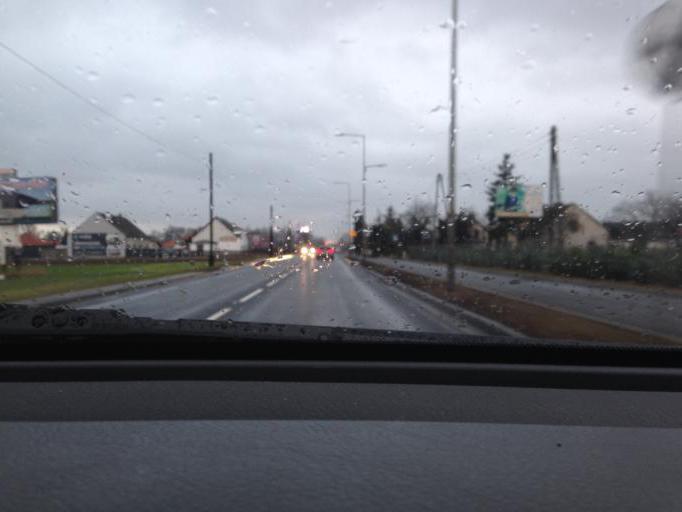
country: PL
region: Opole Voivodeship
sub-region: Powiat opolski
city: Wegry
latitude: 50.7174
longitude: 17.9994
